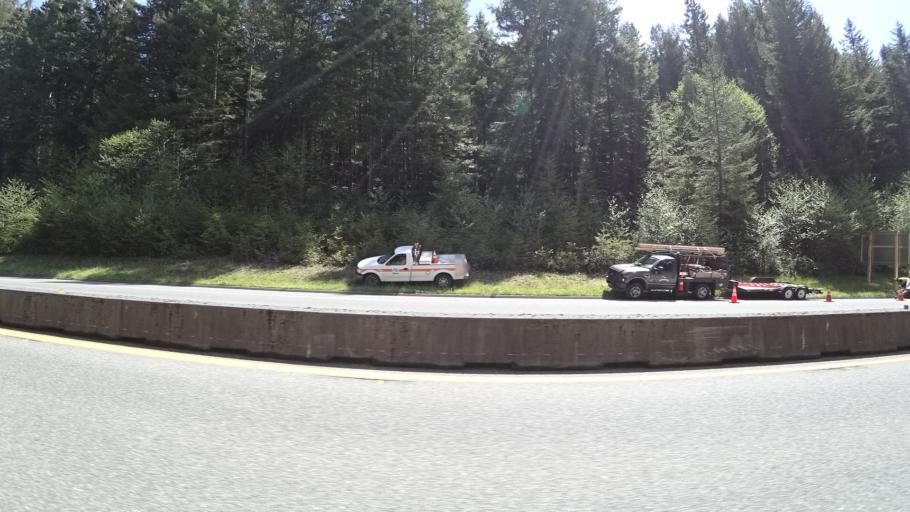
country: US
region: California
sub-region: Humboldt County
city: Westhaven-Moonstone
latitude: 41.3869
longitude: -123.9950
